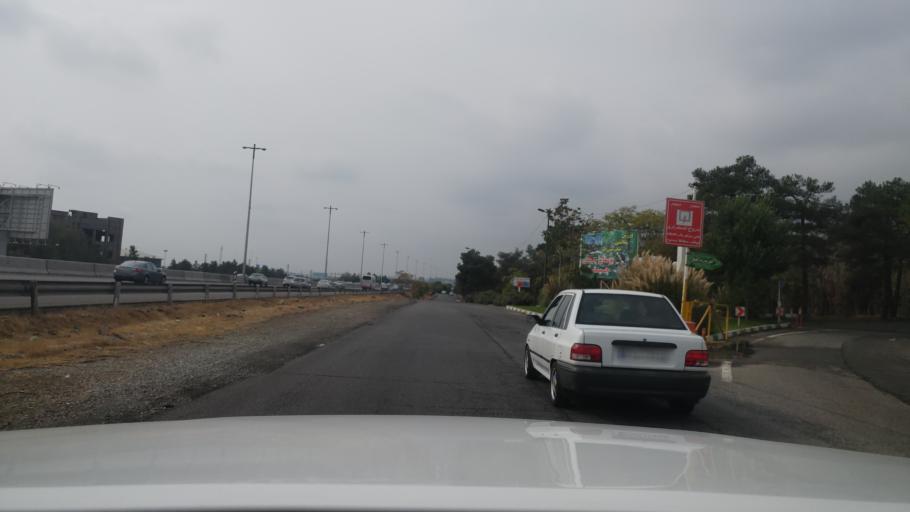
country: IR
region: Tehran
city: Shahr-e Qods
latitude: 35.7187
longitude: 51.2191
